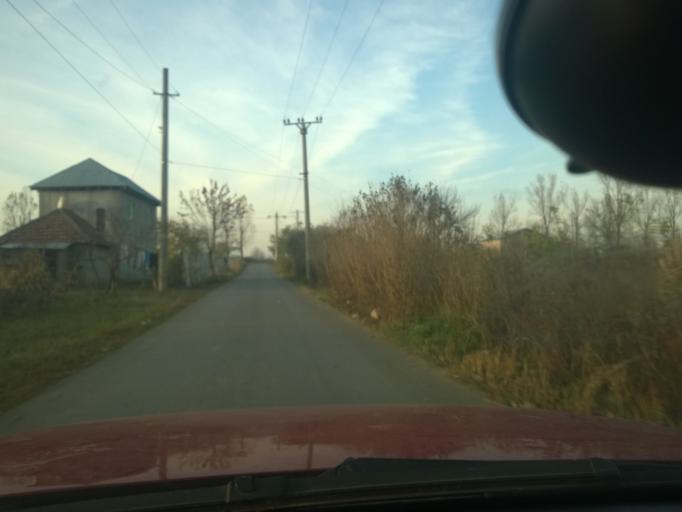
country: RO
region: Giurgiu
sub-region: Comuna Herasti
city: Herasti
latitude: 44.2177
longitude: 26.3576
